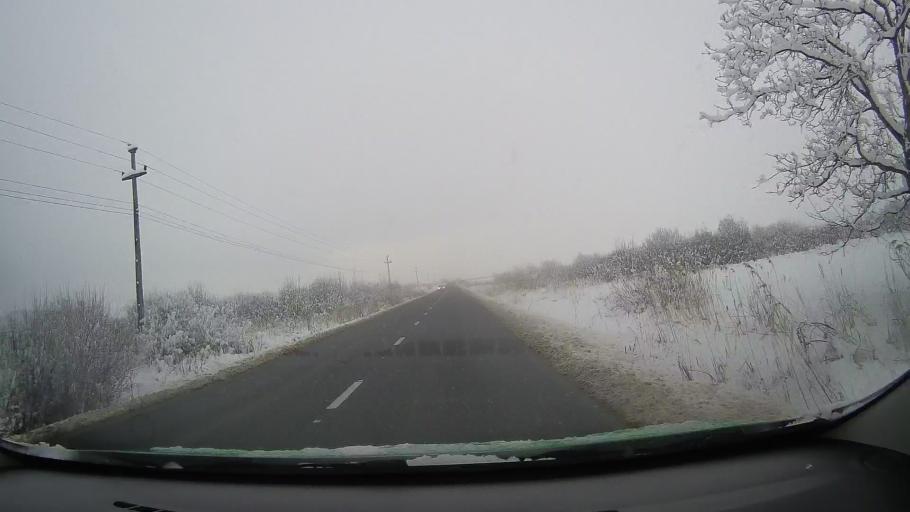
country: RO
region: Sibiu
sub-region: Comuna Cristian
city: Cristian
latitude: 45.7655
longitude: 24.0013
